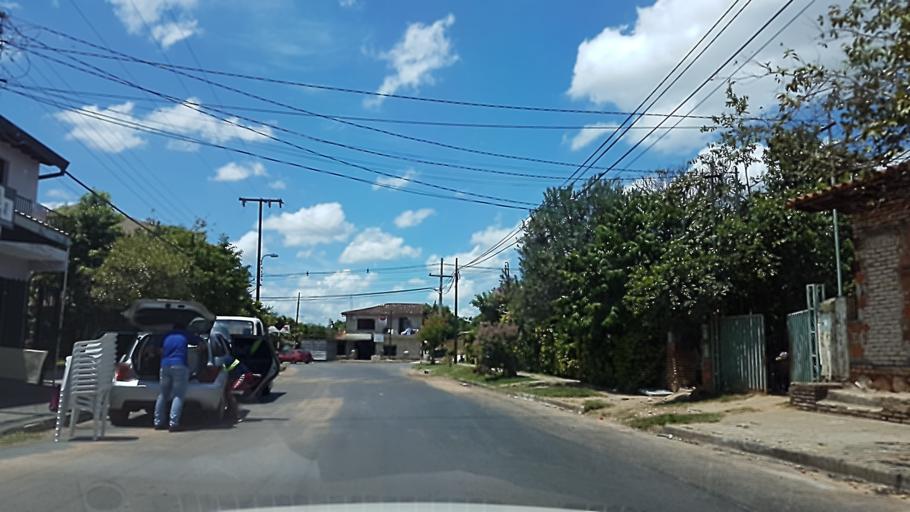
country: PY
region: Central
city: Colonia Mariano Roque Alonso
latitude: -25.2465
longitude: -57.5337
